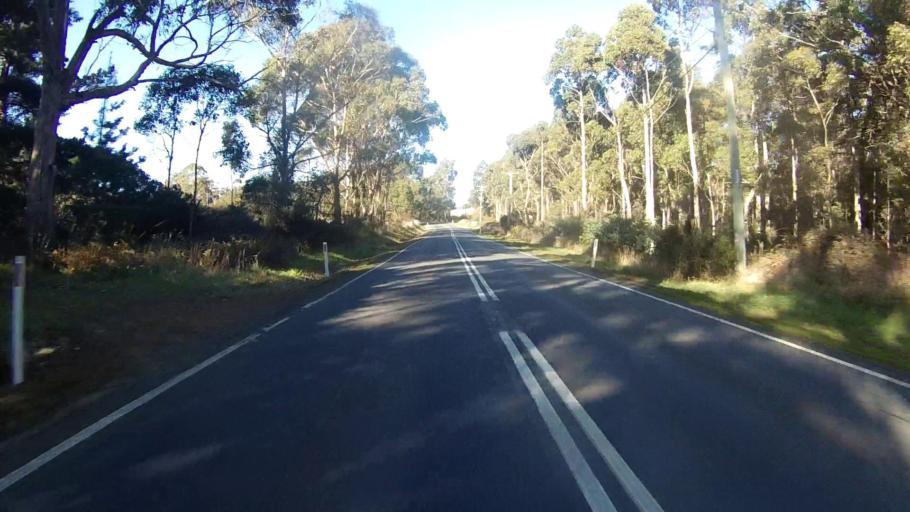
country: AU
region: Tasmania
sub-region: Sorell
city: Sorell
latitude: -42.8208
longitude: 147.8030
